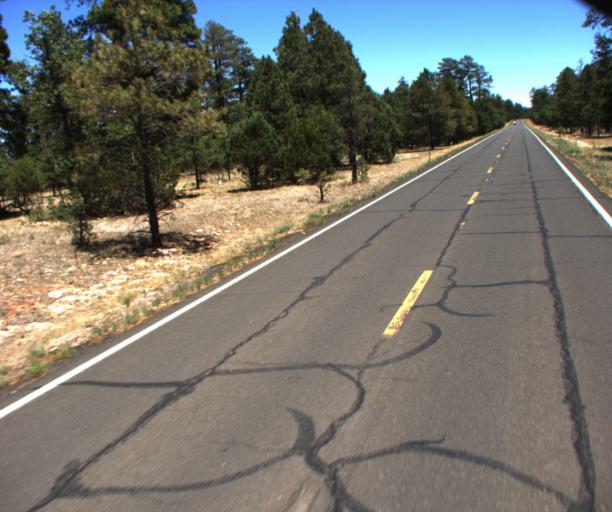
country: US
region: Arizona
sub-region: Gila County
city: Star Valley
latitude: 34.6250
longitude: -111.1499
